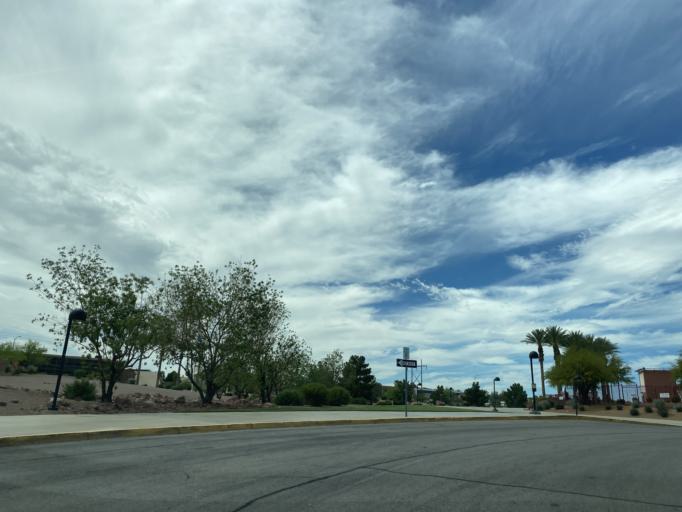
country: US
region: Nevada
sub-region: Clark County
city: Whitney
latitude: 36.0196
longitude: -115.0800
